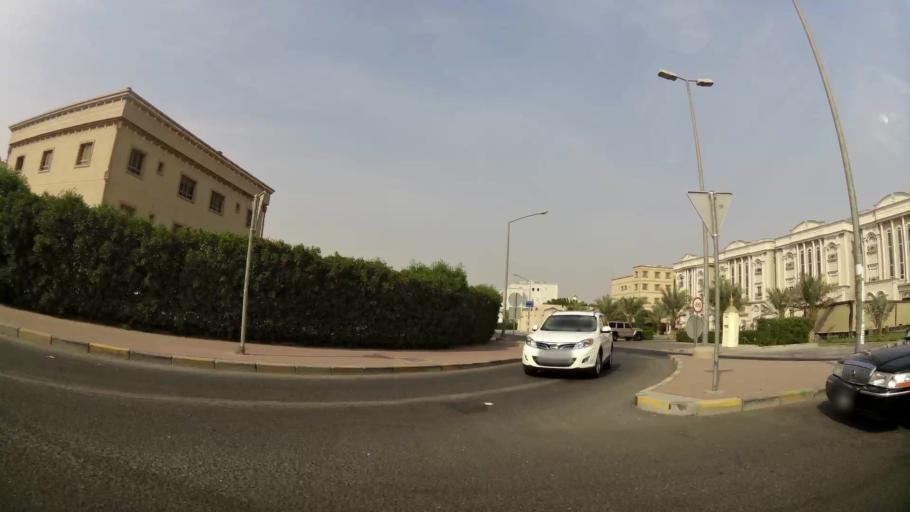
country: KW
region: Al Asimah
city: Ar Rabiyah
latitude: 29.2751
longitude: 47.9287
